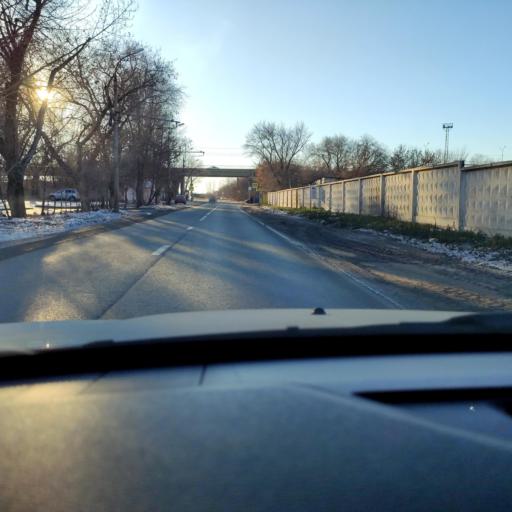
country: RU
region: Samara
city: Samara
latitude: 53.1157
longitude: 50.0652
